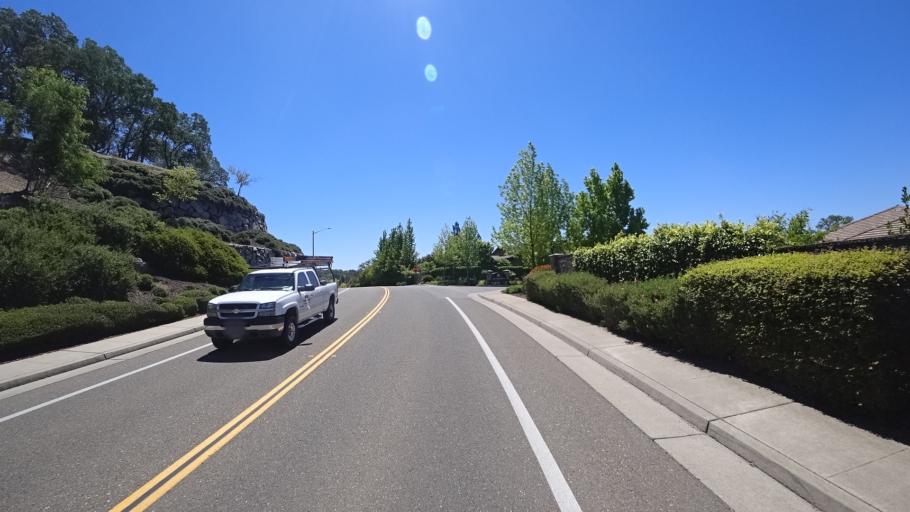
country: US
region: California
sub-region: Placer County
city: Rocklin
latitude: 38.8288
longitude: -121.2473
